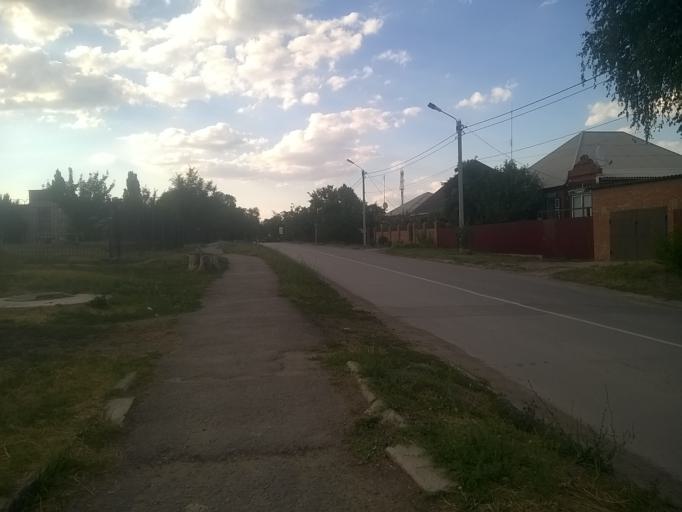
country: RU
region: Rostov
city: Donetsk
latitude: 48.3325
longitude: 39.9526
